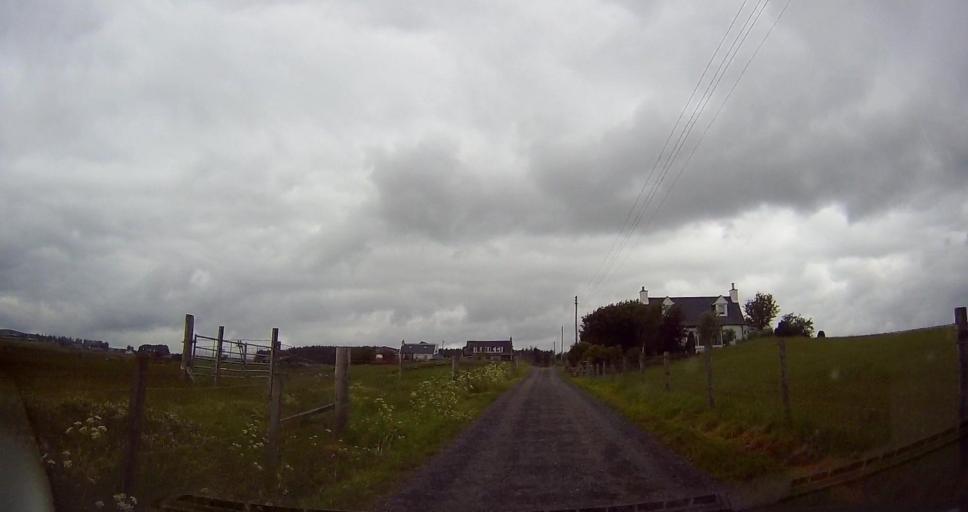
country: GB
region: Scotland
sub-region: Highland
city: Alness
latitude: 58.0619
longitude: -4.4288
